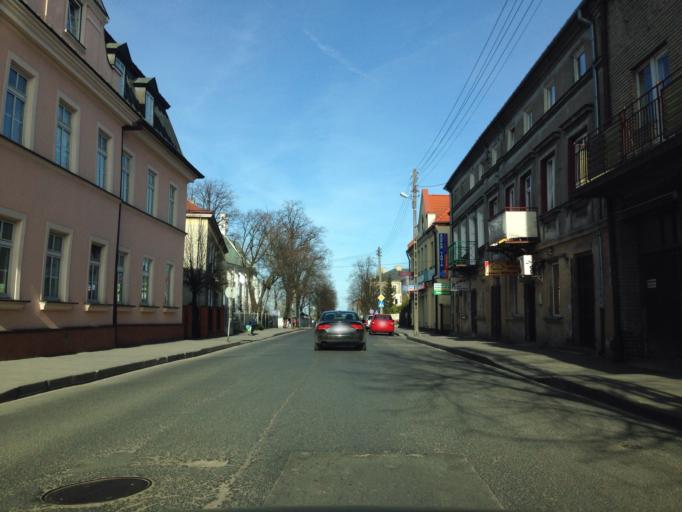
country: PL
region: Lodz Voivodeship
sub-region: Powiat leczycki
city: Leczyca
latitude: 52.0609
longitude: 19.1994
